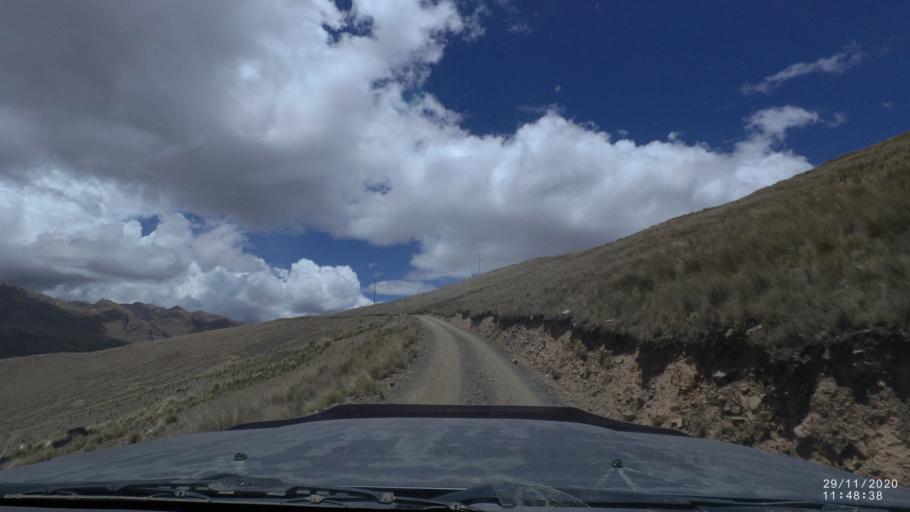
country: BO
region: Cochabamba
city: Cochabamba
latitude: -17.1783
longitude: -66.2573
